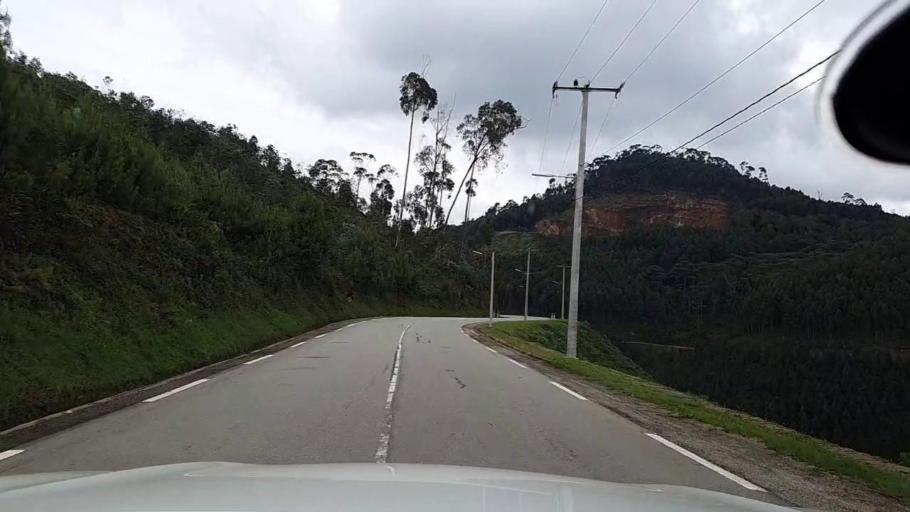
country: RW
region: Southern Province
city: Nzega
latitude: -2.5290
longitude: 29.4063
